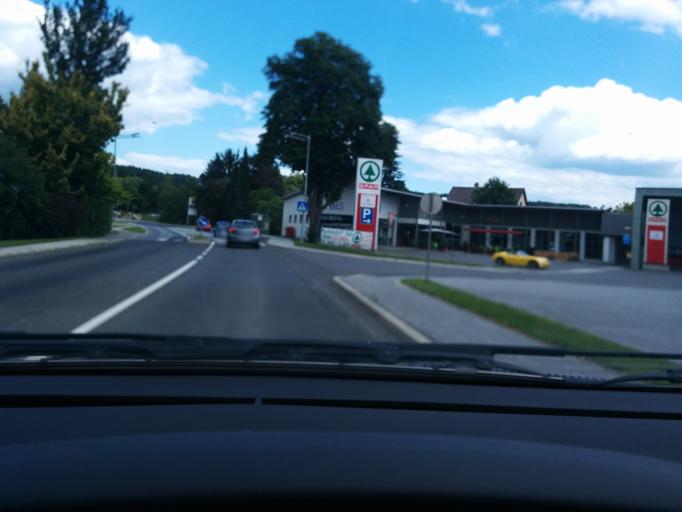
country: AT
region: Styria
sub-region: Politischer Bezirk Weiz
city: Hirnsdorf
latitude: 47.1719
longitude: 15.8064
